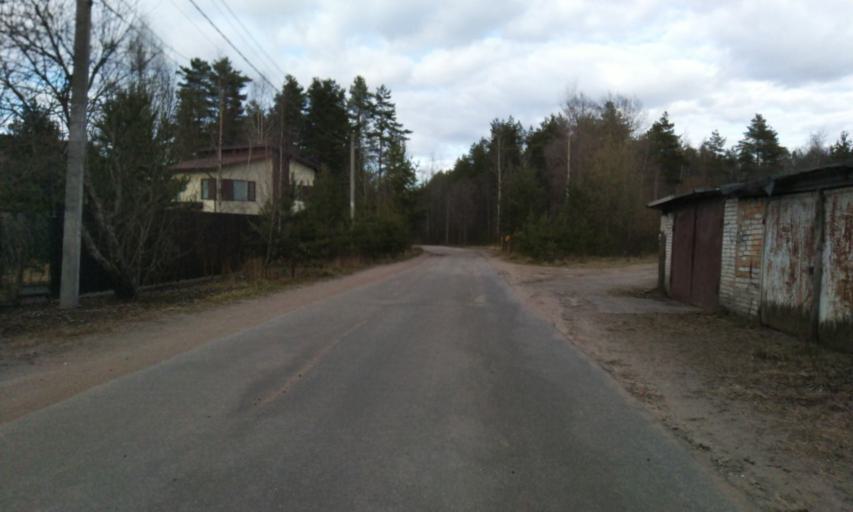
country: RU
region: Leningrad
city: Novoye Devyatkino
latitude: 60.1149
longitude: 30.4789
